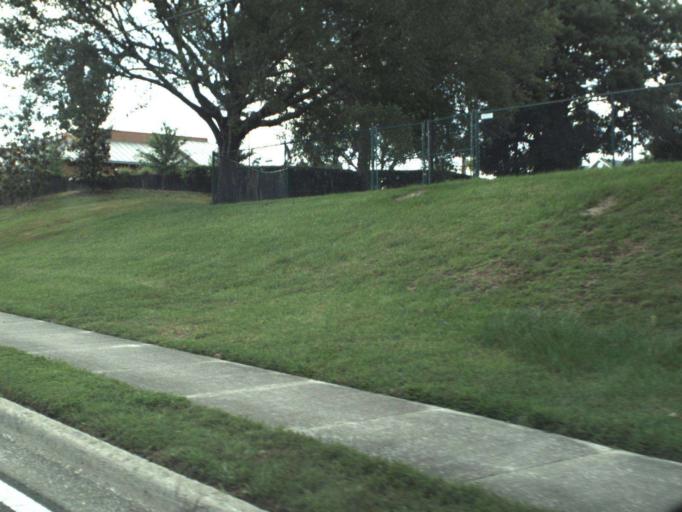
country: US
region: Florida
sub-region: Marion County
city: Ocala
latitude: 29.1718
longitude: -82.1315
